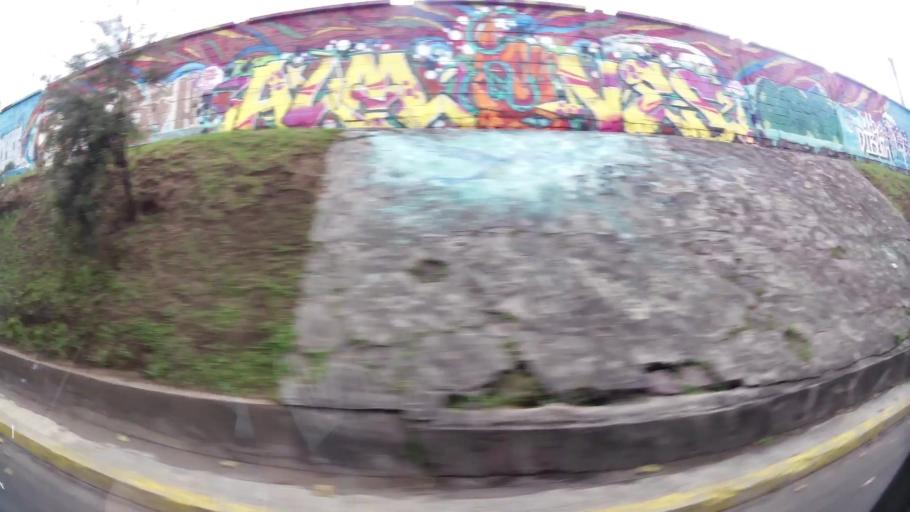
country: EC
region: Pichincha
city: Quito
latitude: -0.1948
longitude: -78.4886
